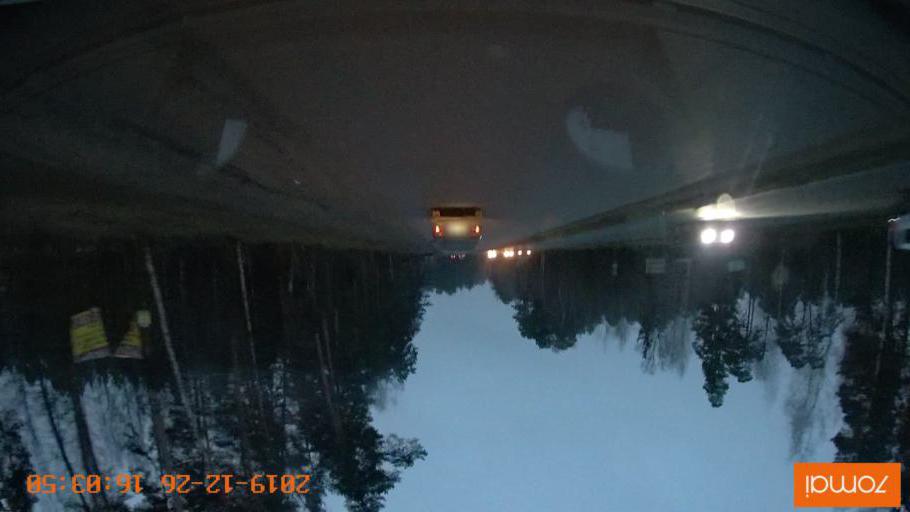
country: RU
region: Jaroslavl
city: Rybinsk
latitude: 58.0101
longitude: 38.8590
